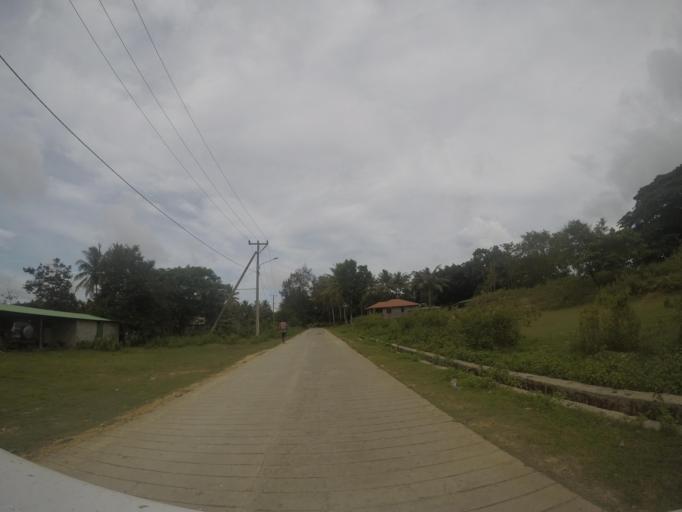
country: TL
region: Lautem
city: Lospalos
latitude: -8.5092
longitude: 126.9858
